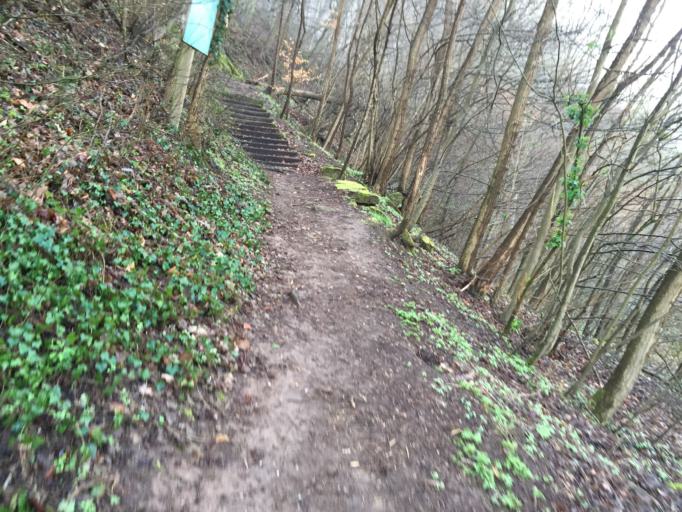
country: DE
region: Rheinland-Pfalz
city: Frankenstein
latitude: 49.4392
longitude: 7.9736
